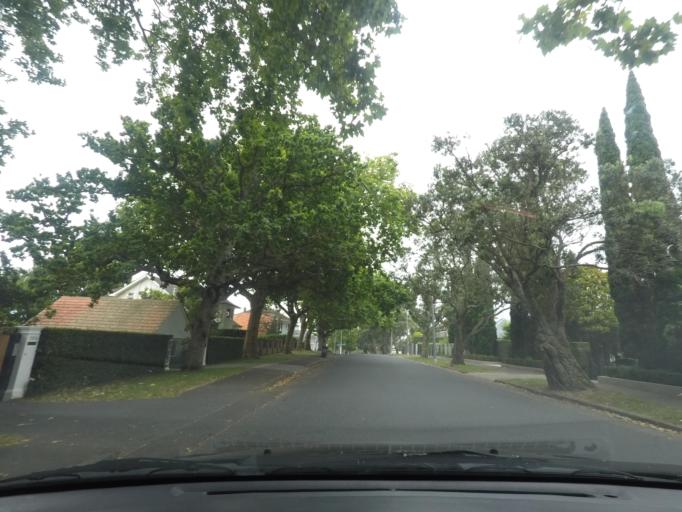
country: NZ
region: Auckland
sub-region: Auckland
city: Auckland
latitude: -36.8533
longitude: 174.7895
